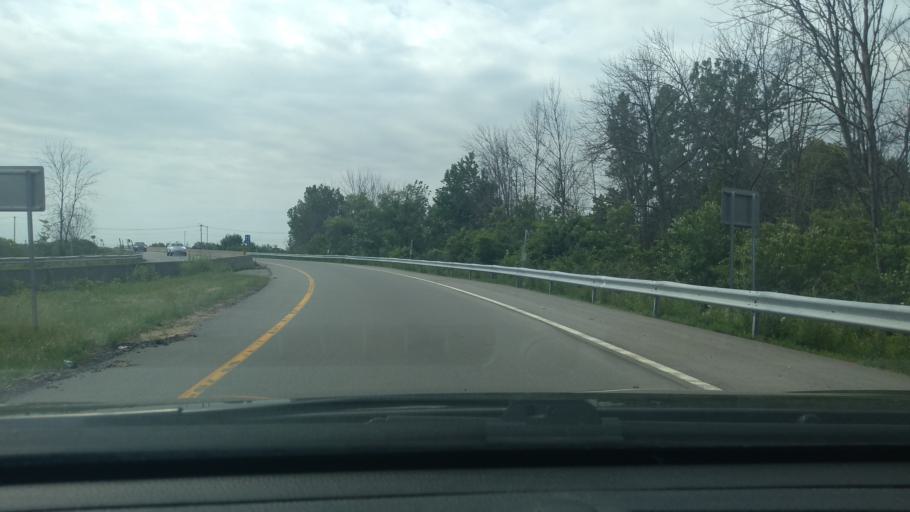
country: US
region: New York
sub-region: Erie County
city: West Seneca
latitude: 42.8304
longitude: -78.7934
